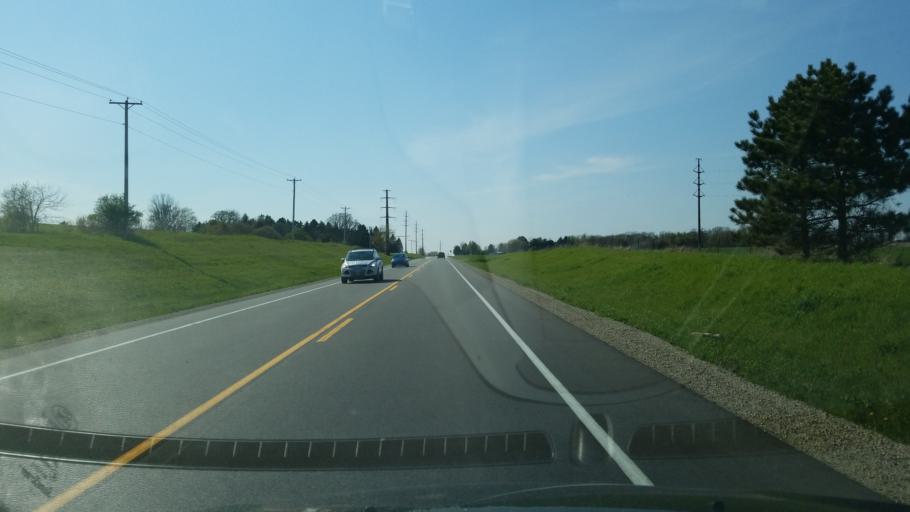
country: US
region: Wisconsin
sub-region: Dane County
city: Fitchburg
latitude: 42.9639
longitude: -89.4865
